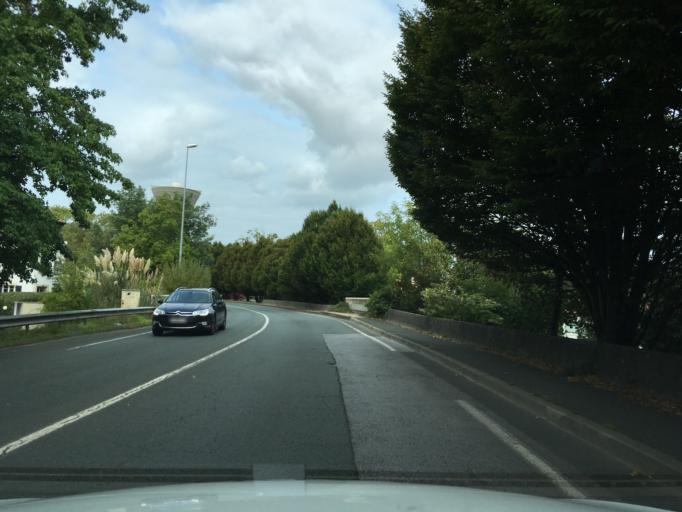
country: FR
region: Aquitaine
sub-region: Departement des Pyrenees-Atlantiques
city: Bayonne
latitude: 43.4805
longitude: -1.4572
